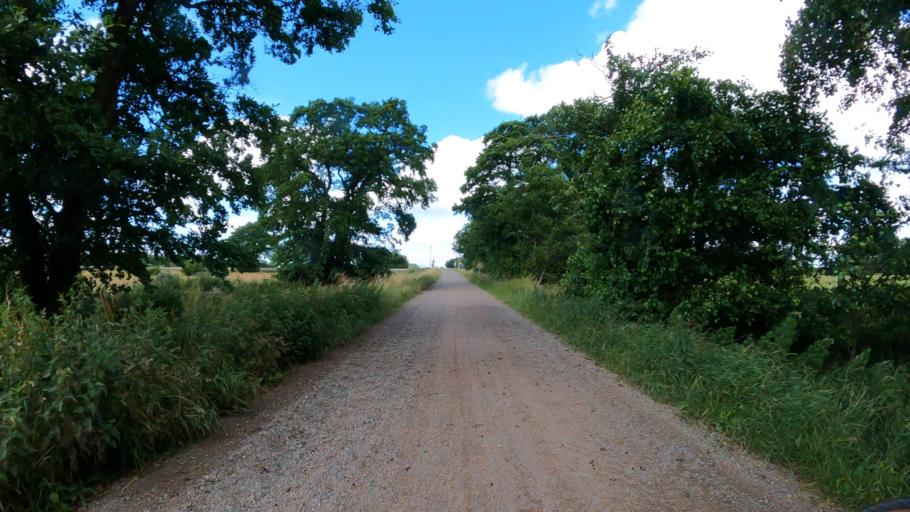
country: DE
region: Lower Saxony
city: Neu Wulmstorf
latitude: 53.4701
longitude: 9.7580
